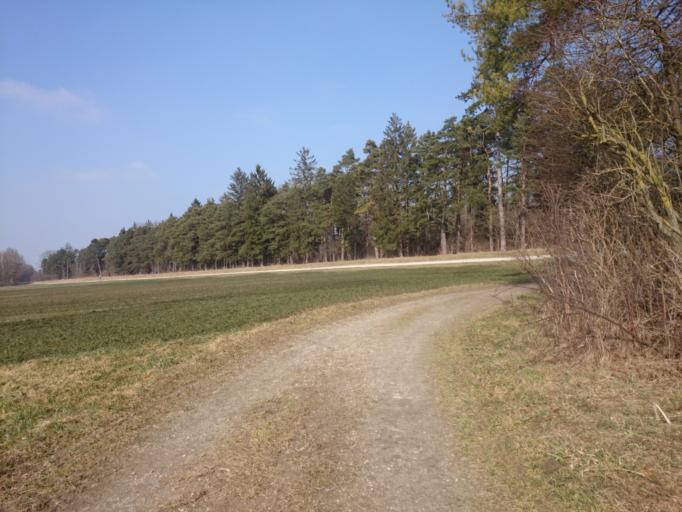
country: DE
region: Bavaria
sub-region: Swabia
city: Konigsbrunn
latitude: 48.2854
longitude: 10.9115
